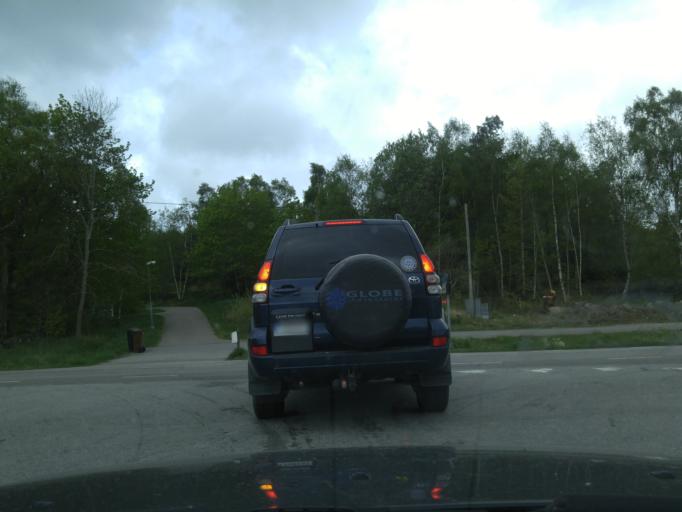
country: SE
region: Vaestra Goetaland
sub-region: Stenungsunds Kommun
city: Stora Hoga
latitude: 57.9910
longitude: 11.8304
